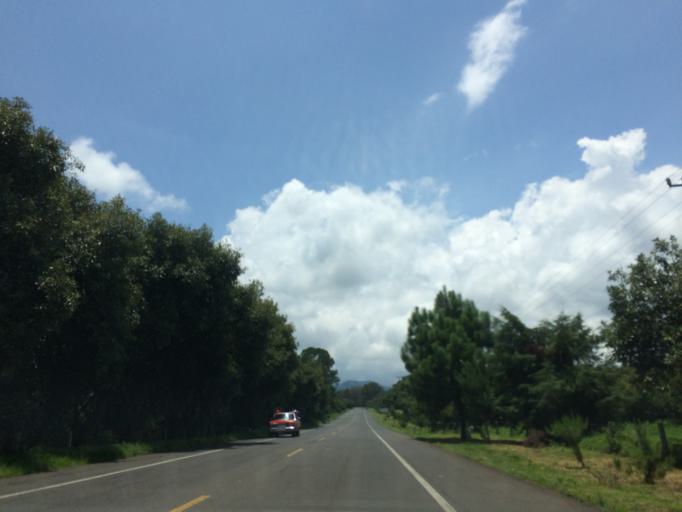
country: MX
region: Michoacan
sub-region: Periban
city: San Francisco Periban
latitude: 19.5551
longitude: -102.3896
